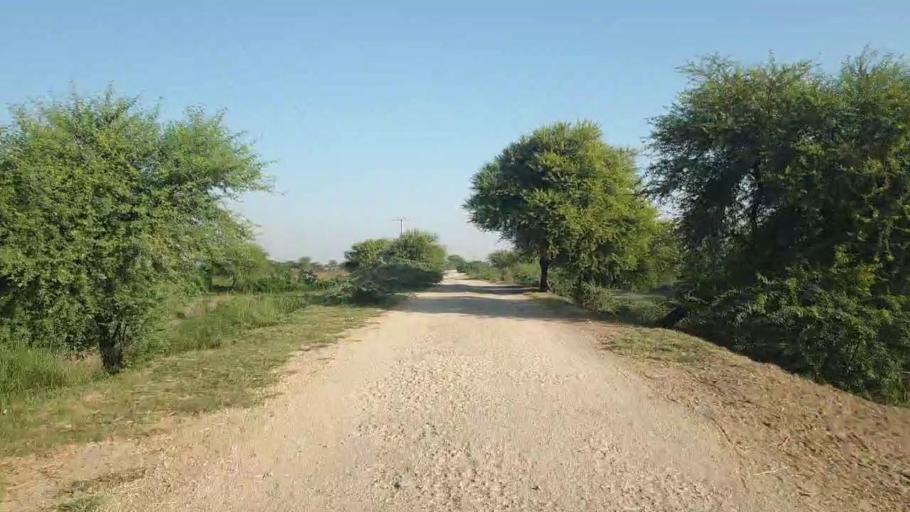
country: PK
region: Sindh
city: Badin
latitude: 24.6931
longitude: 68.8160
